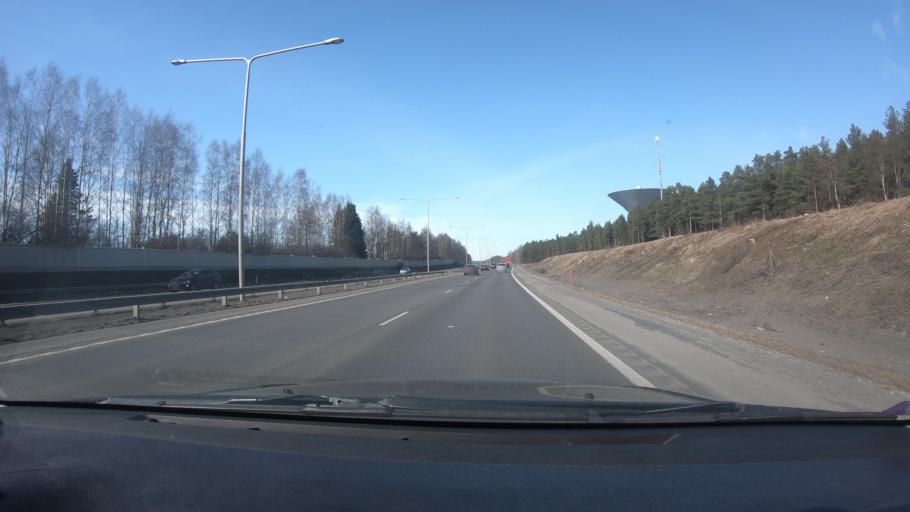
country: FI
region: Northern Ostrobothnia
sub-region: Oulu
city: Oulu
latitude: 65.0343
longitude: 25.4897
